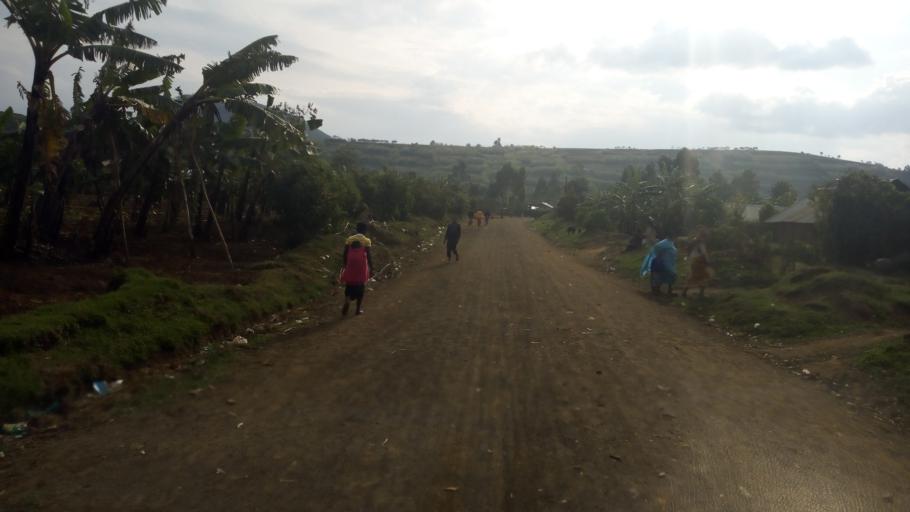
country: UG
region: Western Region
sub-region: Kisoro District
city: Kisoro
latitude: -1.3025
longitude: 29.7053
